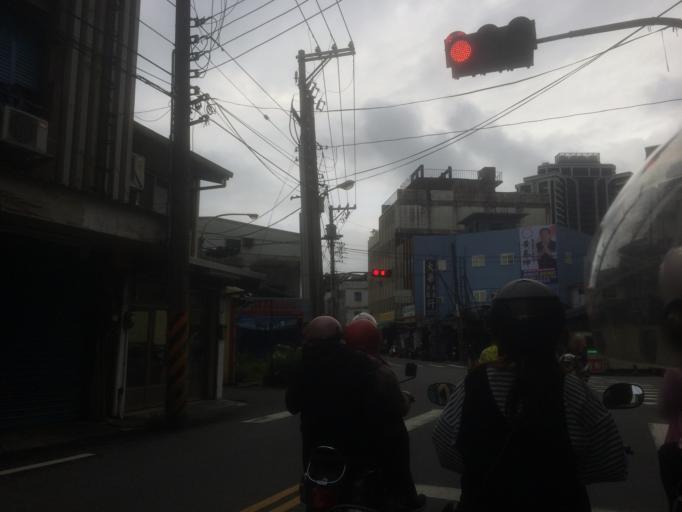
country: TW
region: Taiwan
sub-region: Yilan
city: Yilan
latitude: 24.6744
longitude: 121.7720
